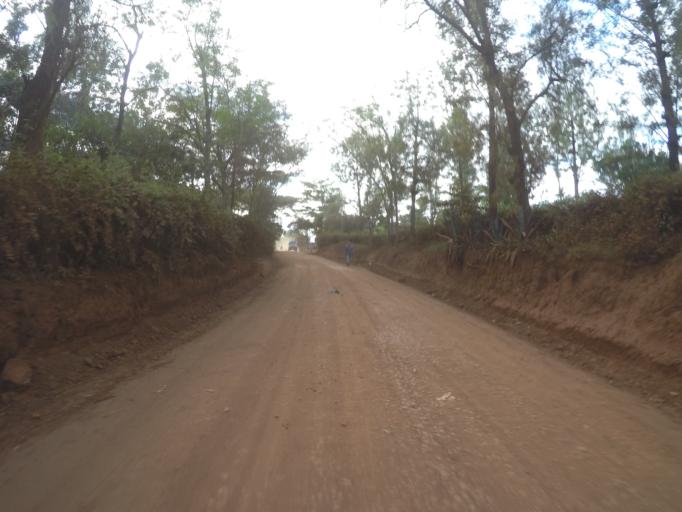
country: TZ
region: Arusha
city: Kiratu
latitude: -3.3262
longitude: 35.6656
